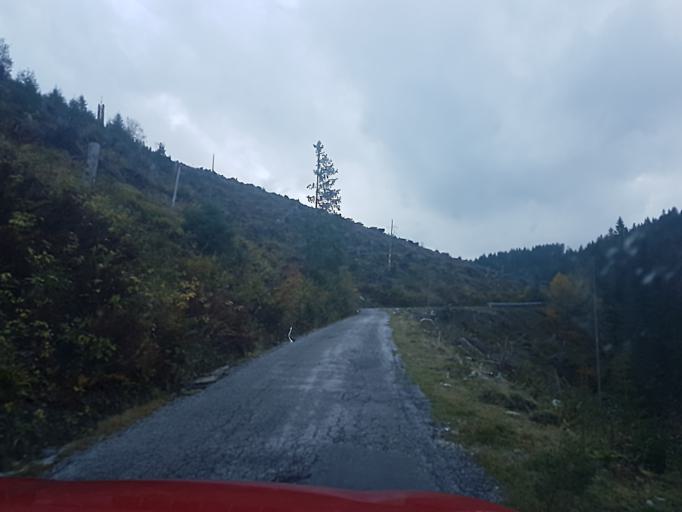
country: SK
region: Zilinsky
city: Ruzomberok
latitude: 48.9967
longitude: 19.2171
